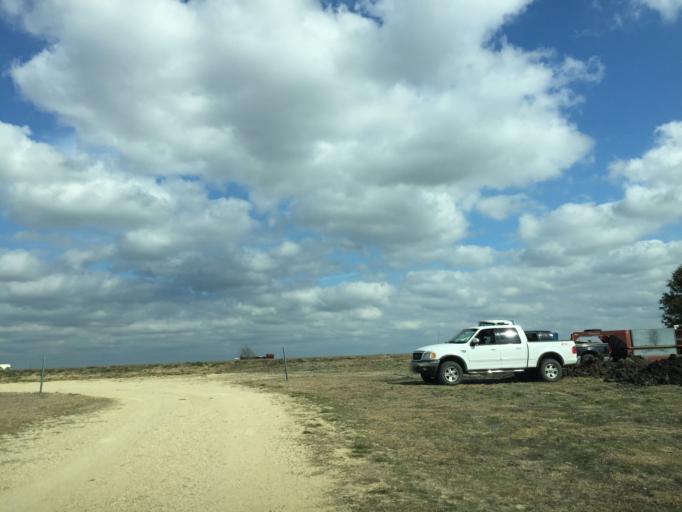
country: US
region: Texas
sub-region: Williamson County
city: Granger
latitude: 30.7188
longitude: -97.4249
